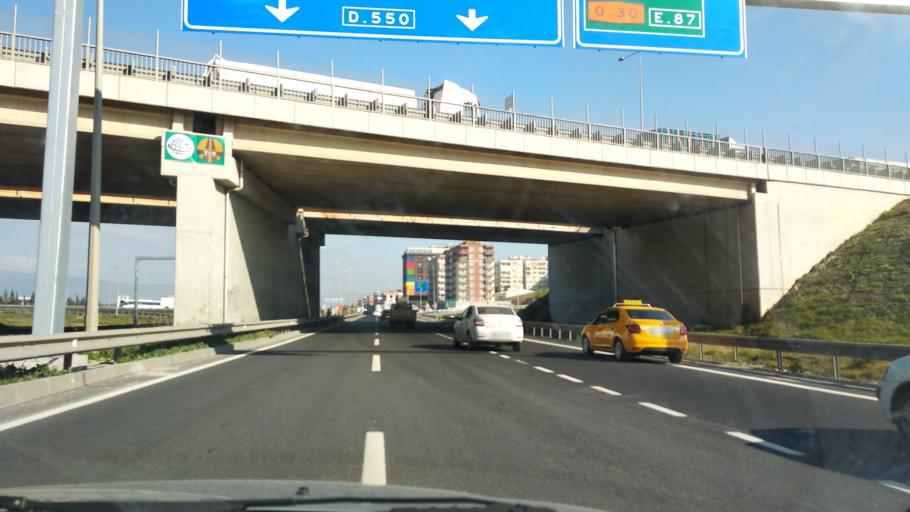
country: TR
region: Izmir
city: Menemen
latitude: 38.5705
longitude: 27.0566
